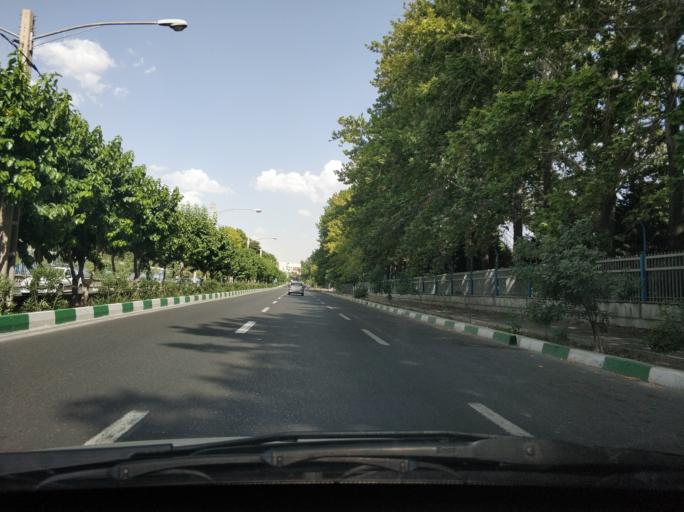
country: IR
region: Tehran
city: Tehran
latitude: 35.7433
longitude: 51.5820
